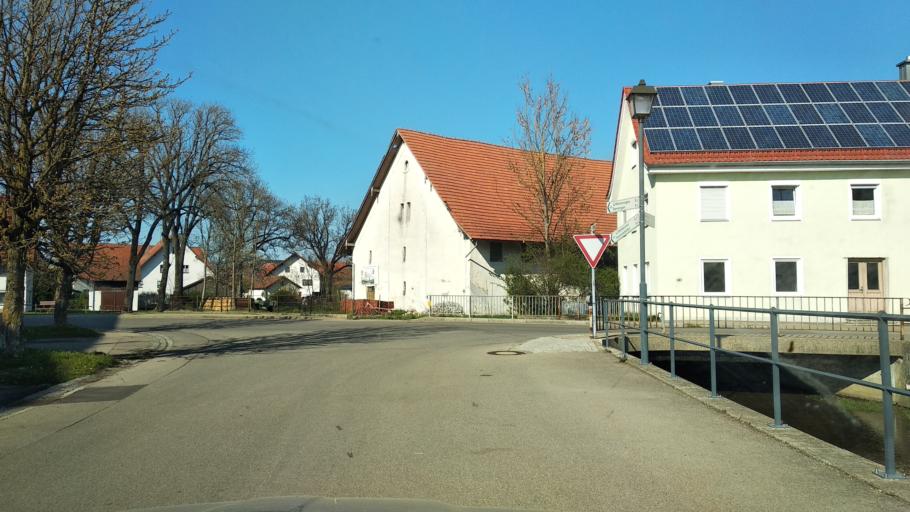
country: DE
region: Bavaria
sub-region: Swabia
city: Hawangen
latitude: 47.9705
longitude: 10.2631
